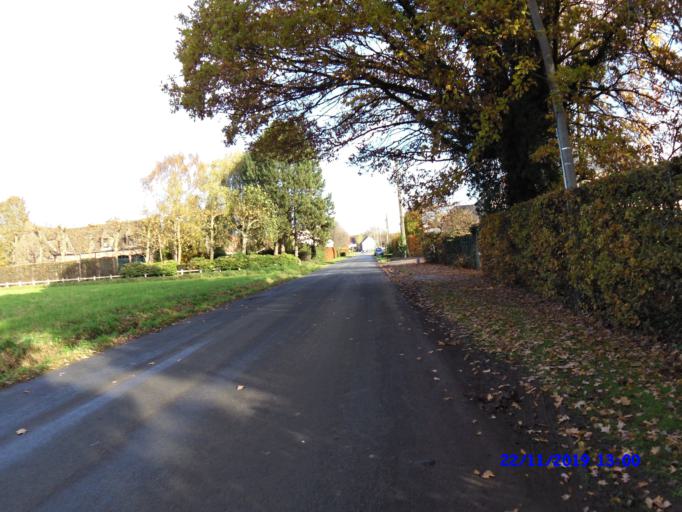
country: BE
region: Flanders
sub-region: Provincie Vlaams-Brabant
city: Londerzeel
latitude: 50.9826
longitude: 4.2961
